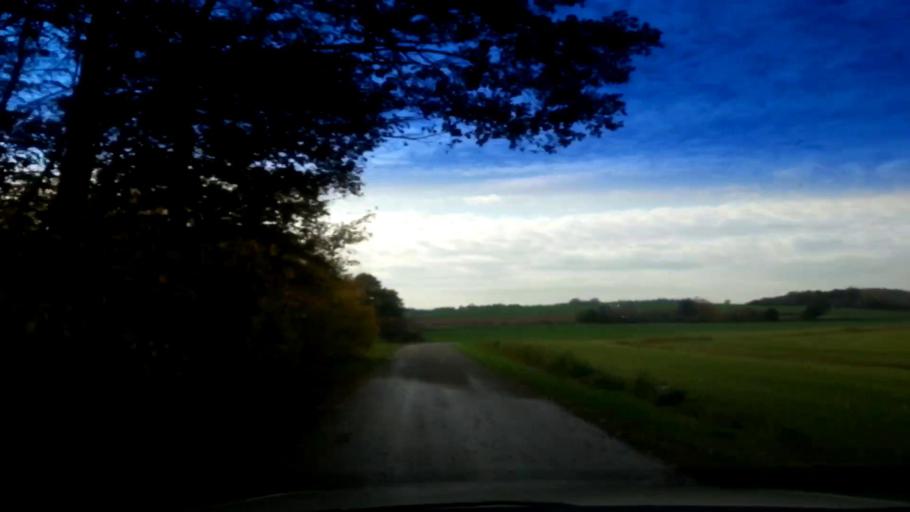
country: DE
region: Bavaria
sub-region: Upper Franconia
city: Stegaurach
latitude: 49.8500
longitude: 10.8718
